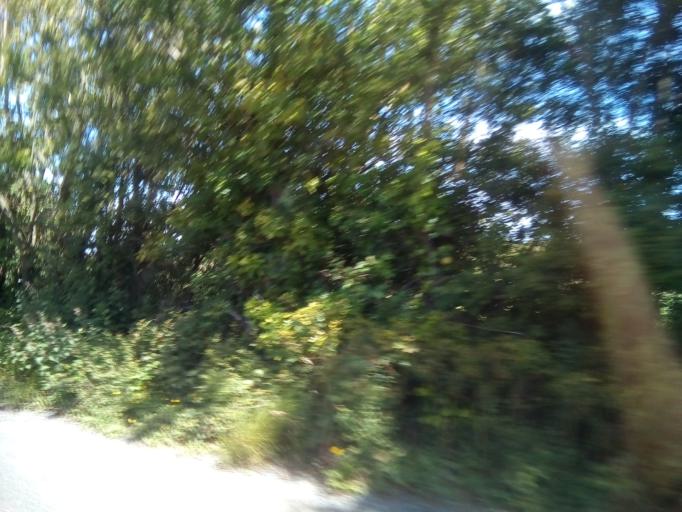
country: IE
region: Leinster
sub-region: Loch Garman
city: Loch Garman
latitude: 52.2332
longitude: -6.5660
